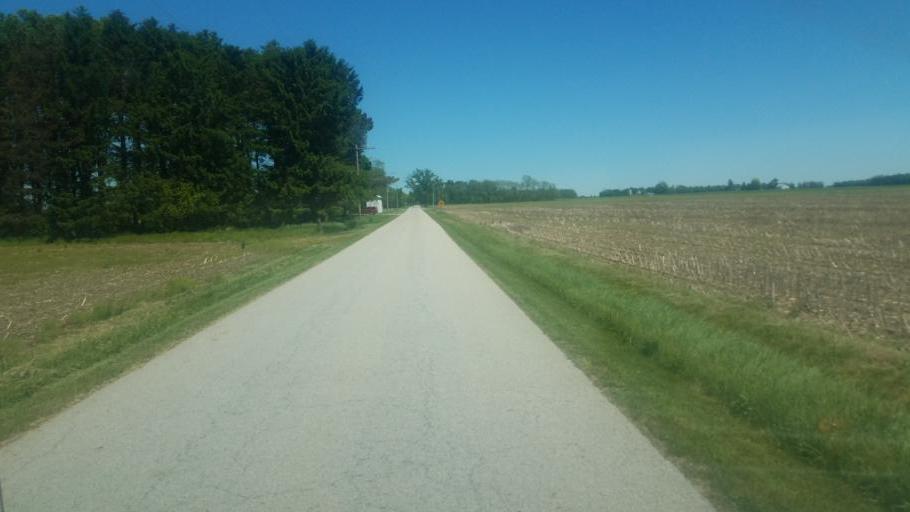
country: US
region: Ohio
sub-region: Champaign County
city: Saint Paris
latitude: 40.1994
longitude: -84.0439
